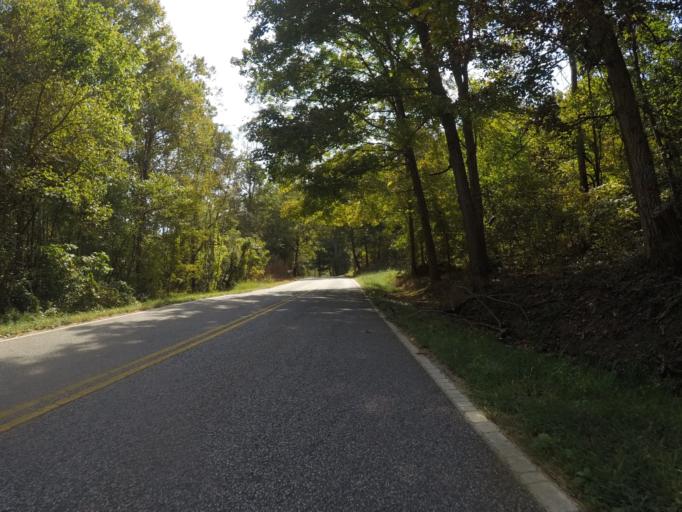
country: US
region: West Virginia
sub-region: Cabell County
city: Lesage
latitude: 38.5847
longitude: -82.4230
